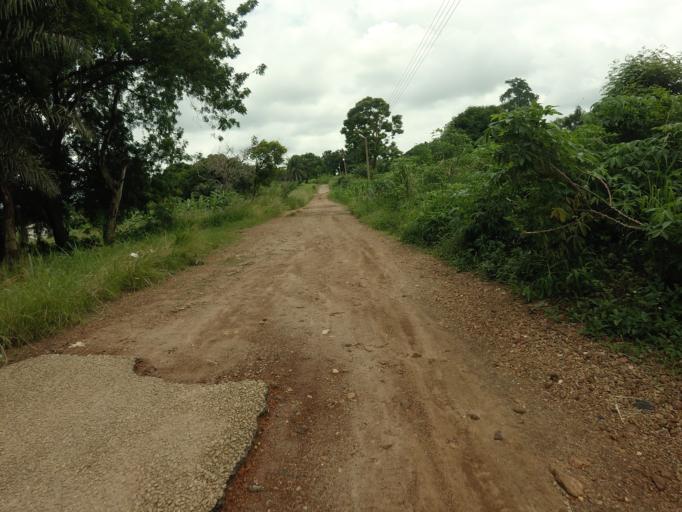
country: GH
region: Volta
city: Ho
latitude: 6.6039
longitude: 0.4613
